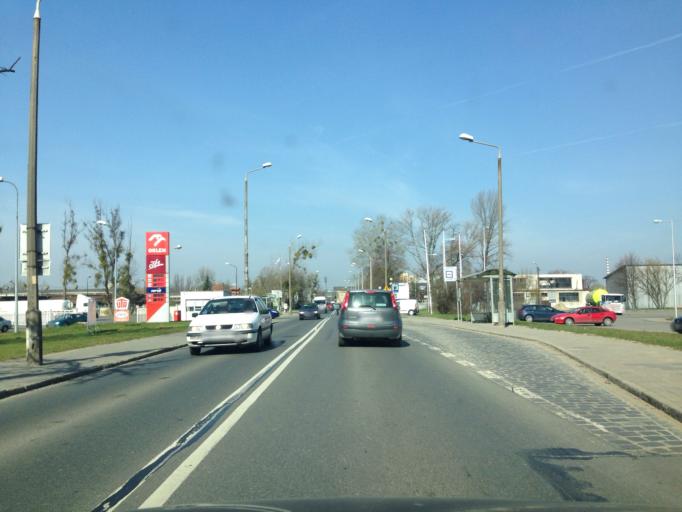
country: PL
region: Lower Silesian Voivodeship
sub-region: Powiat wroclawski
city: Wilczyce
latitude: 51.1139
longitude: 17.1176
